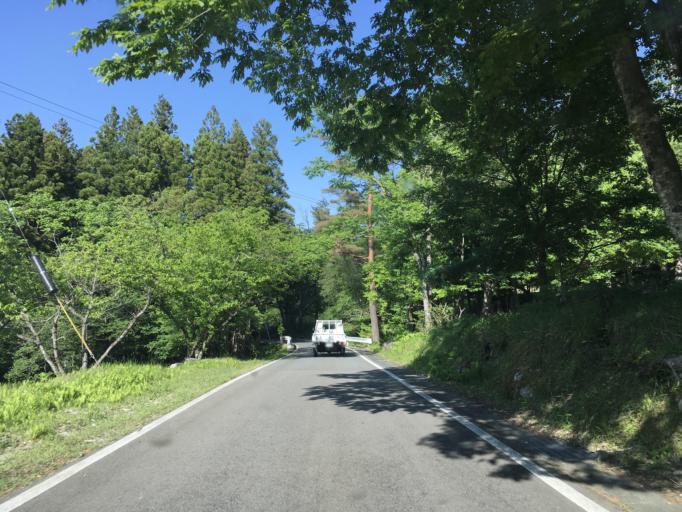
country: JP
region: Iwate
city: Kamaishi
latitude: 39.1941
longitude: 141.8177
